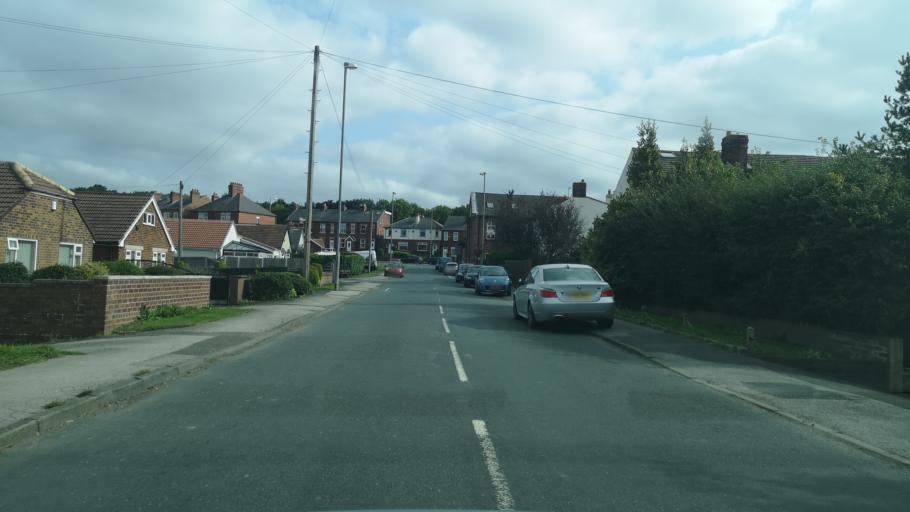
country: GB
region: England
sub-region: City and Borough of Wakefield
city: Crigglestone
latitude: 53.6398
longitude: -1.5407
